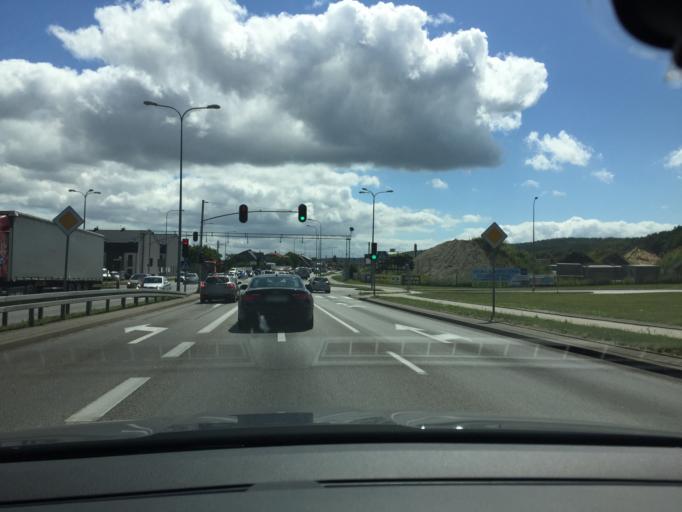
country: PL
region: Pomeranian Voivodeship
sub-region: Powiat wejherowski
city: Reda
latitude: 54.5901
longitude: 18.3586
